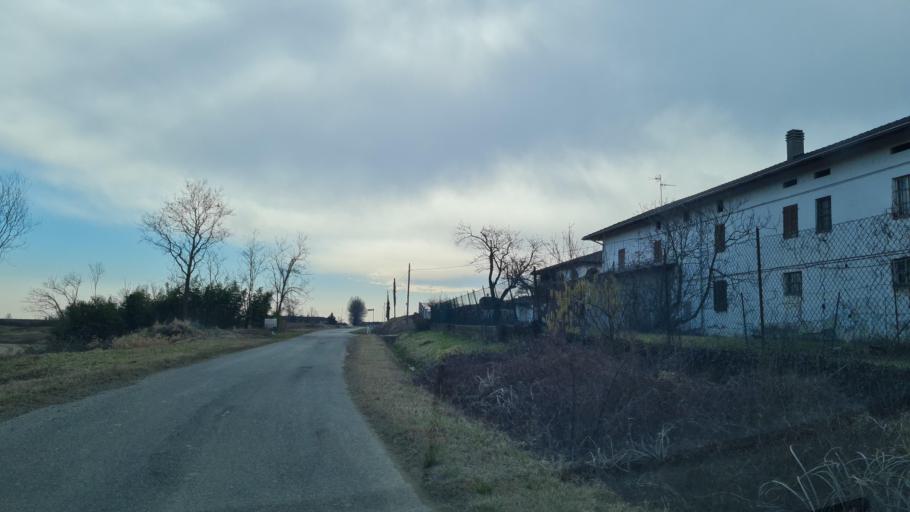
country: IT
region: Piedmont
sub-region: Provincia di Vercelli
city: Buronzo
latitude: 45.4728
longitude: 8.2442
